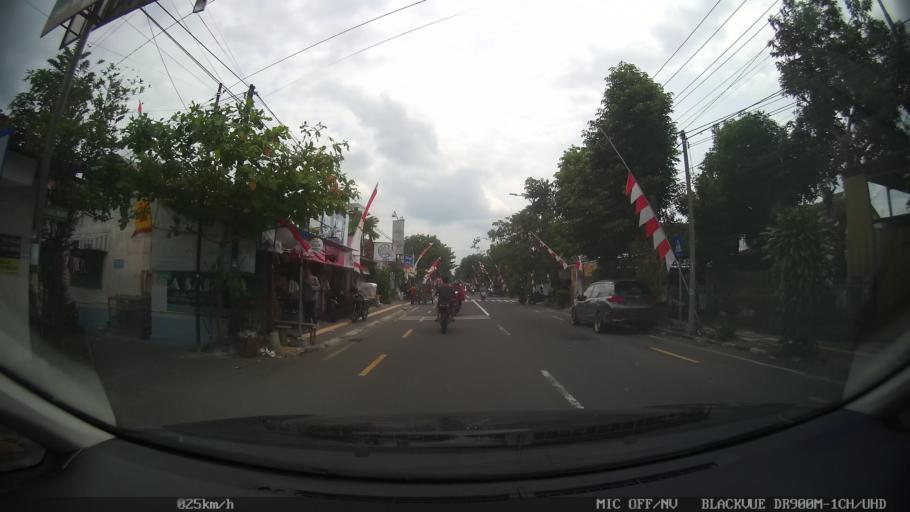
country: ID
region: Daerah Istimewa Yogyakarta
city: Yogyakarta
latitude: -7.7992
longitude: 110.3904
